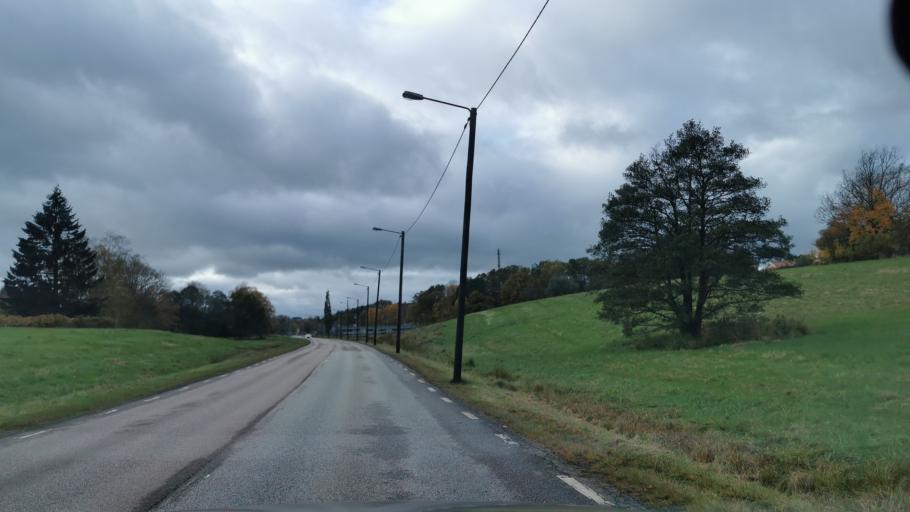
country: SE
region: Vaestra Goetaland
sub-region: Partille Kommun
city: Partille
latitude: 57.7236
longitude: 12.0871
